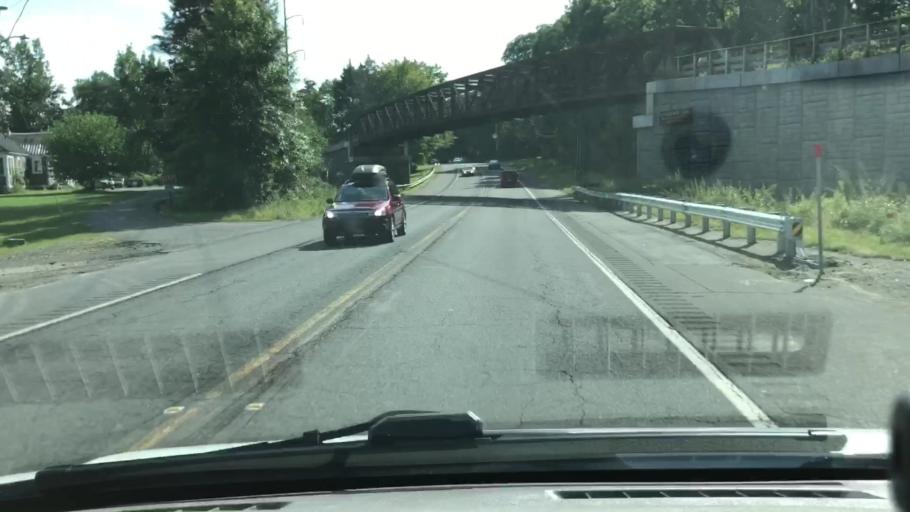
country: US
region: Massachusetts
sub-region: Hampshire County
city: Northampton
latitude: 42.3006
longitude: -72.6560
